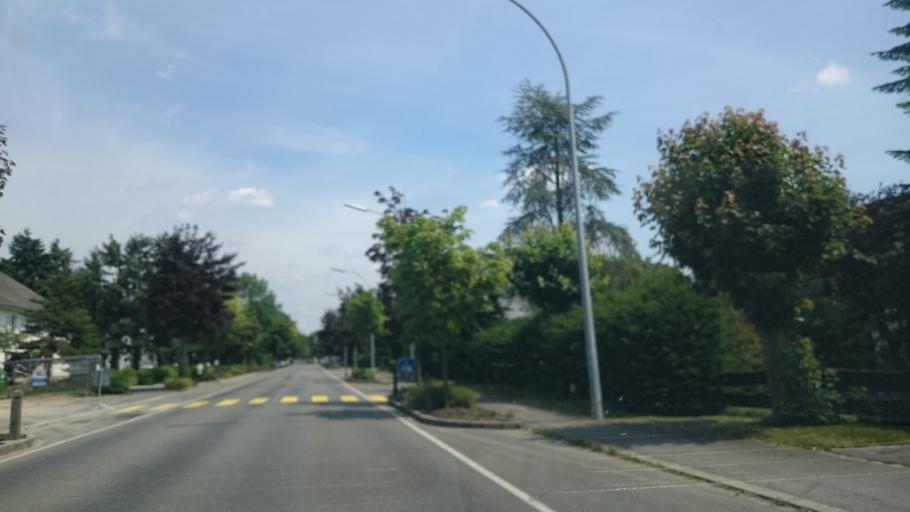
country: LU
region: Luxembourg
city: Capellen
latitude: 49.6461
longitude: 5.9796
